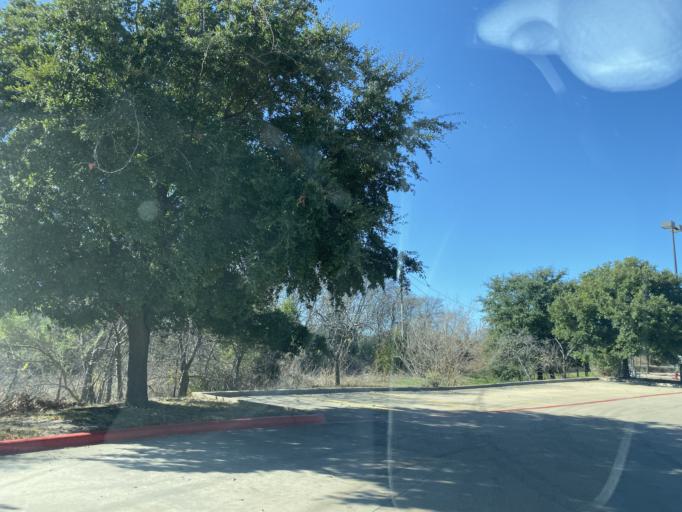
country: US
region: Texas
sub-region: Travis County
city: Windemere
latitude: 30.4753
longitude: -97.6698
